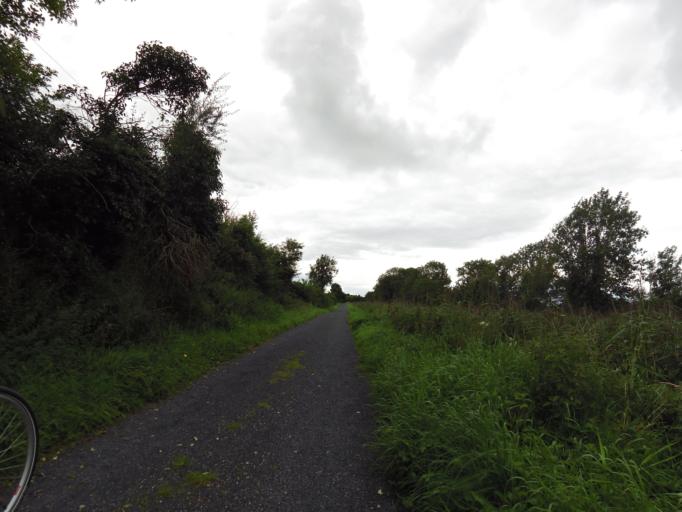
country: IE
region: Leinster
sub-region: An Iarmhi
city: An Muileann gCearr
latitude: 53.5478
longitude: -7.4747
